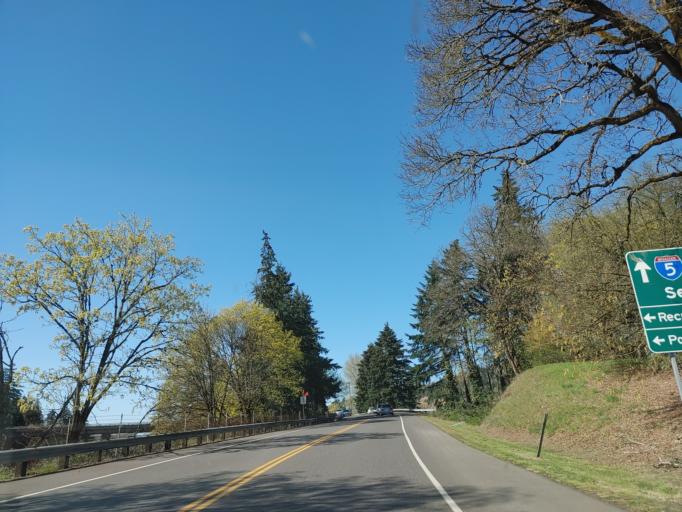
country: US
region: Washington
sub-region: Cowlitz County
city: Kalama
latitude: 46.0171
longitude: -122.8487
